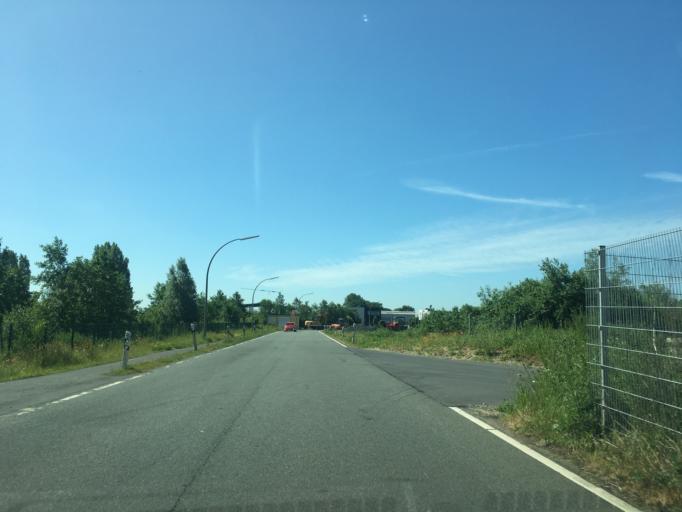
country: DE
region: North Rhine-Westphalia
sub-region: Regierungsbezirk Munster
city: Altenberge
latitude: 52.0354
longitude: 7.4569
